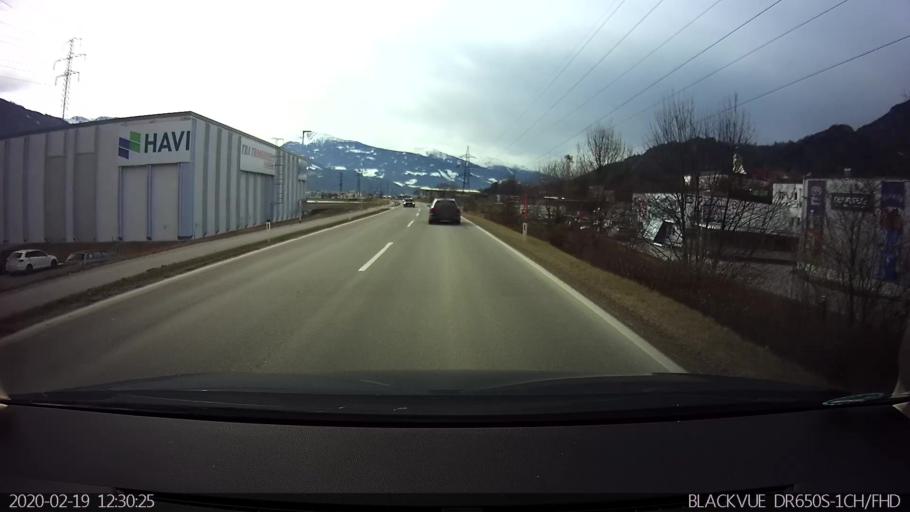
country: AT
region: Tyrol
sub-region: Politischer Bezirk Schwaz
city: Schwaz
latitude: 47.3567
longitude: 11.7029
